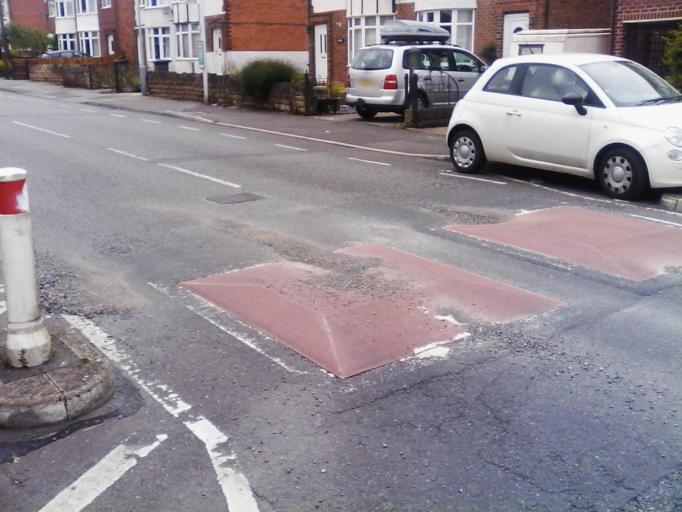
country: GB
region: England
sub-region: Nottinghamshire
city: Arnold
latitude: 52.9717
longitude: -1.1092
